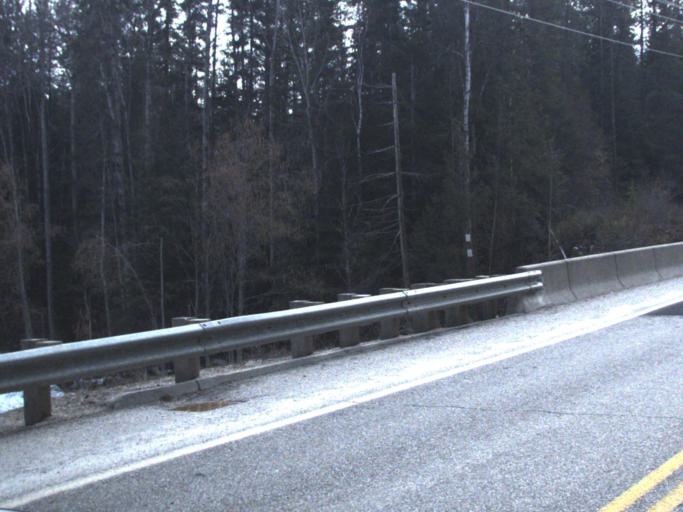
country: US
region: Washington
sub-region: Stevens County
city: Chewelah
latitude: 48.6115
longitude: -117.3654
